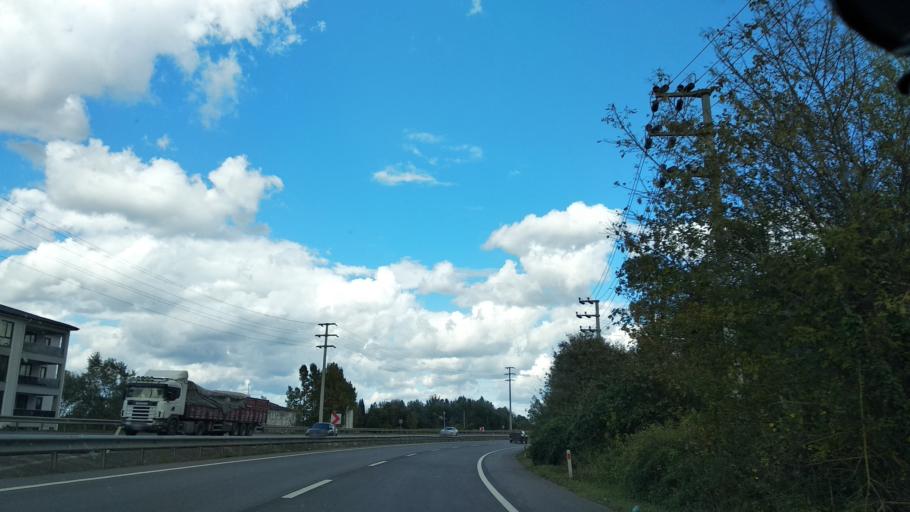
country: TR
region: Sakarya
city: Sogutlu
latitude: 40.8926
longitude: 30.4698
